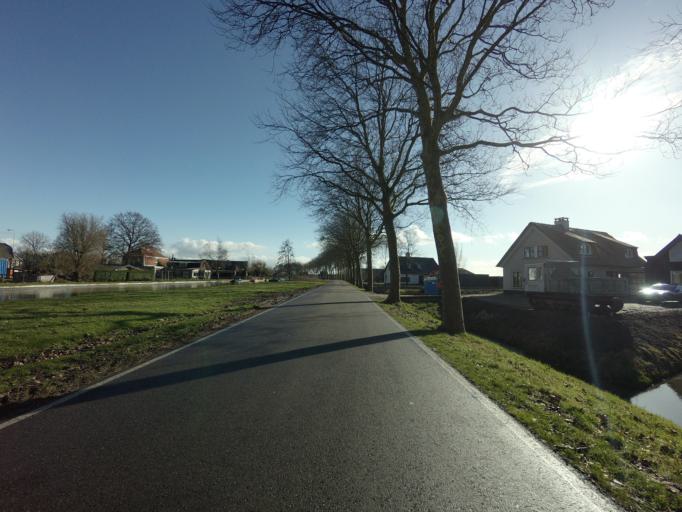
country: NL
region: Utrecht
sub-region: Gemeente Montfoort
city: Montfoort
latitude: 52.0956
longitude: 4.9438
